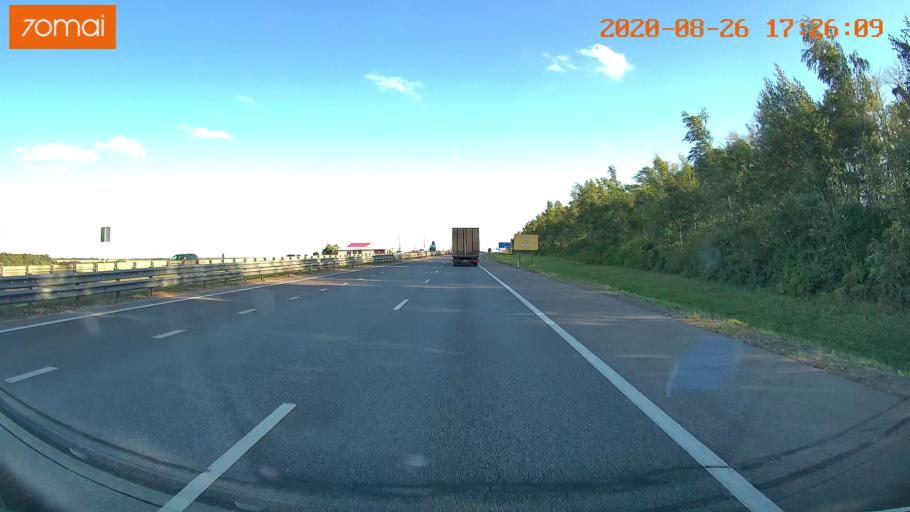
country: RU
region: Tula
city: Volovo
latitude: 53.4905
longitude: 38.1149
